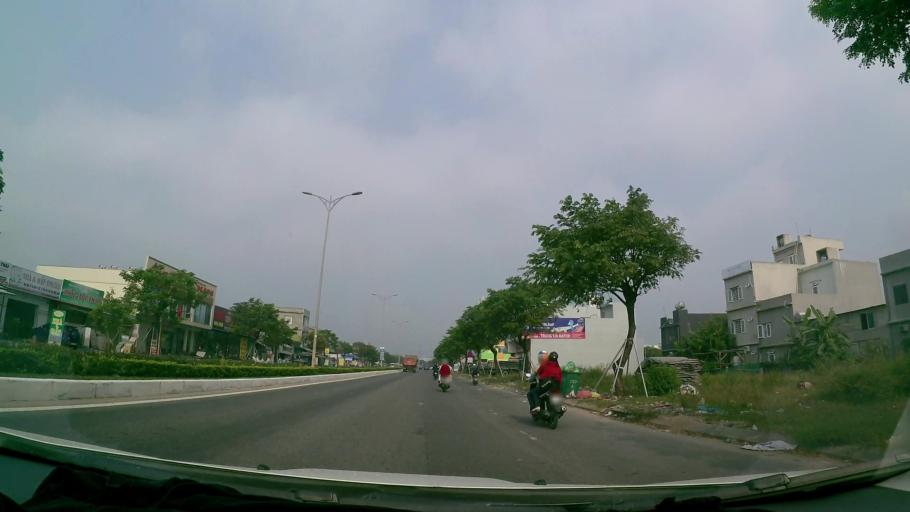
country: VN
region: Da Nang
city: Cam Le
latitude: 16.0035
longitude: 108.2255
